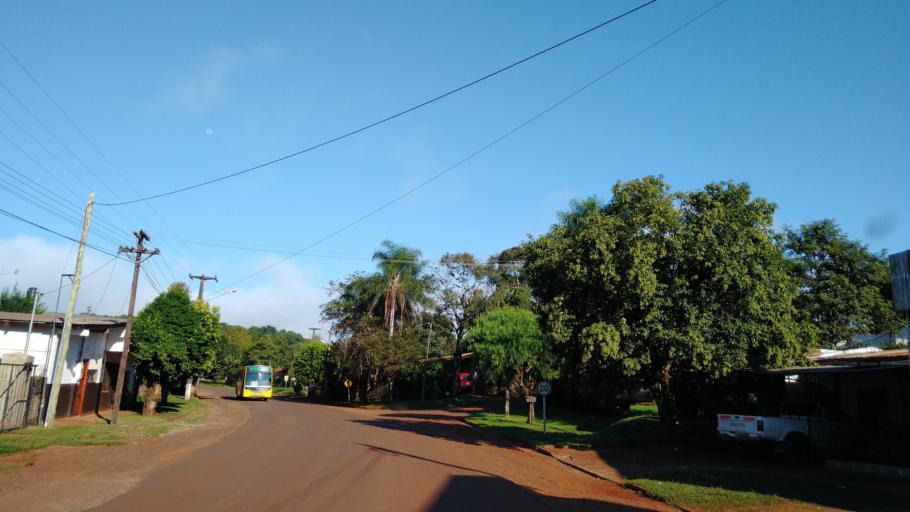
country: AR
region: Misiones
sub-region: Departamento de Montecarlo
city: Montecarlo
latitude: -26.5609
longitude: -54.7791
